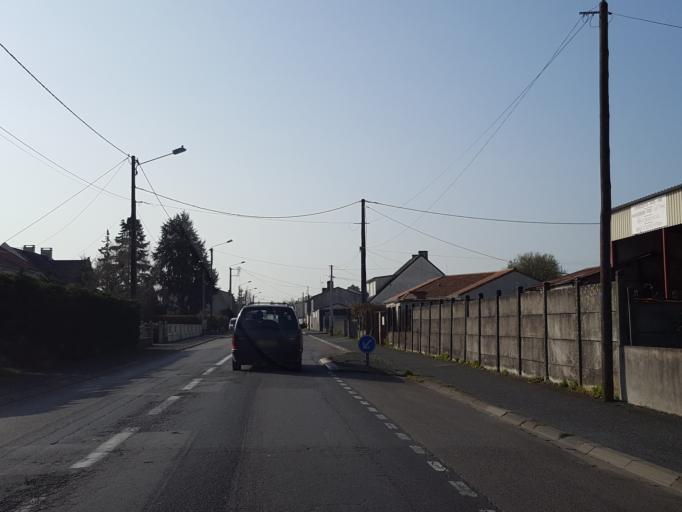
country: FR
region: Pays de la Loire
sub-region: Departement de la Loire-Atlantique
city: Geneston
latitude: 47.0611
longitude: -1.5156
